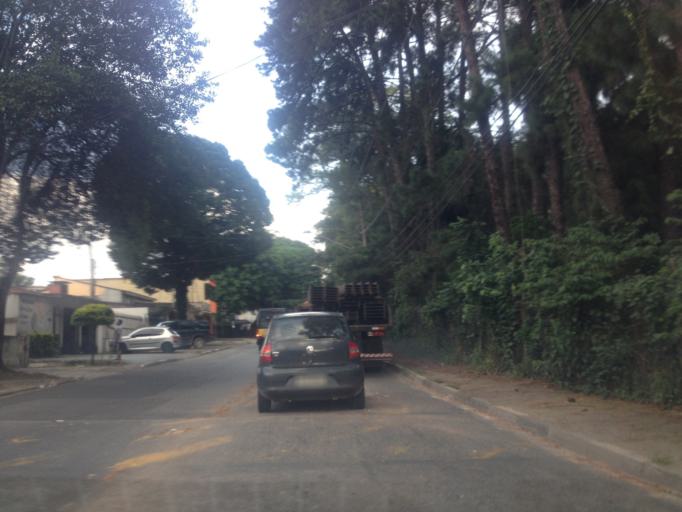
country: BR
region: Sao Paulo
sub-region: Diadema
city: Diadema
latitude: -23.7266
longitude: -46.7171
